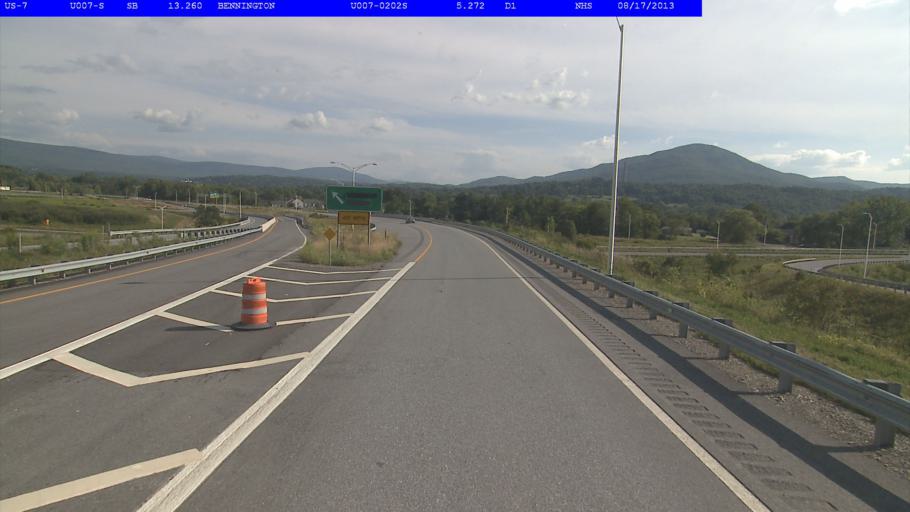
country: US
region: Vermont
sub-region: Bennington County
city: Bennington
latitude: 42.9074
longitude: -73.2086
